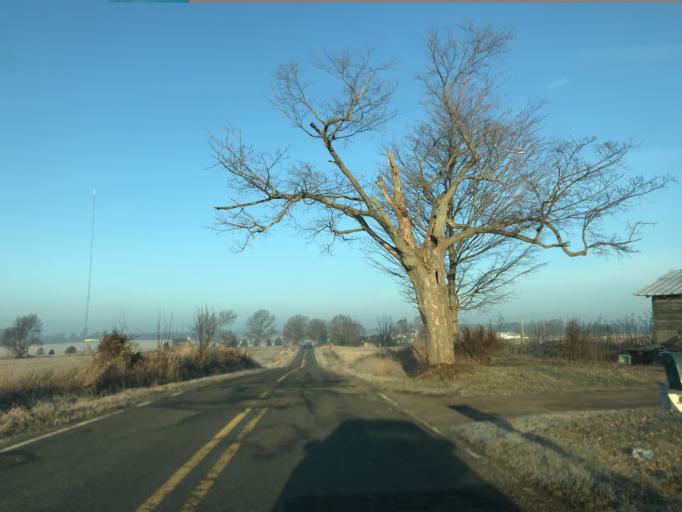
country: US
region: Michigan
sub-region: Ingham County
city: Leslie
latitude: 42.4172
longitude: -84.5090
